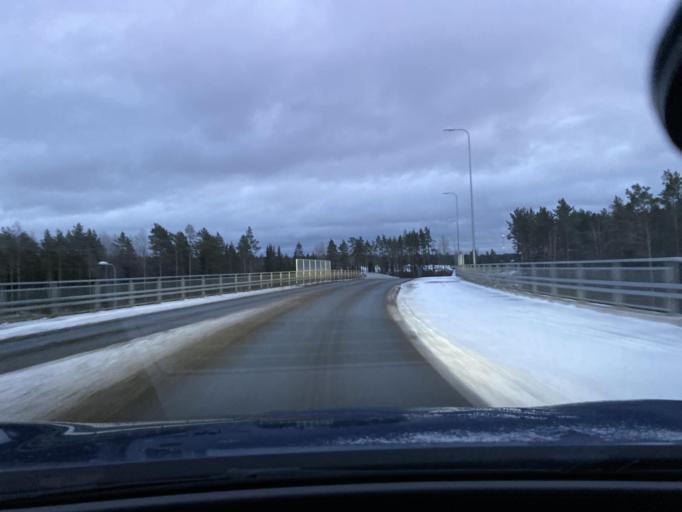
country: FI
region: Satakunta
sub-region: Rauma
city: Rauma
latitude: 61.1492
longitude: 21.5707
